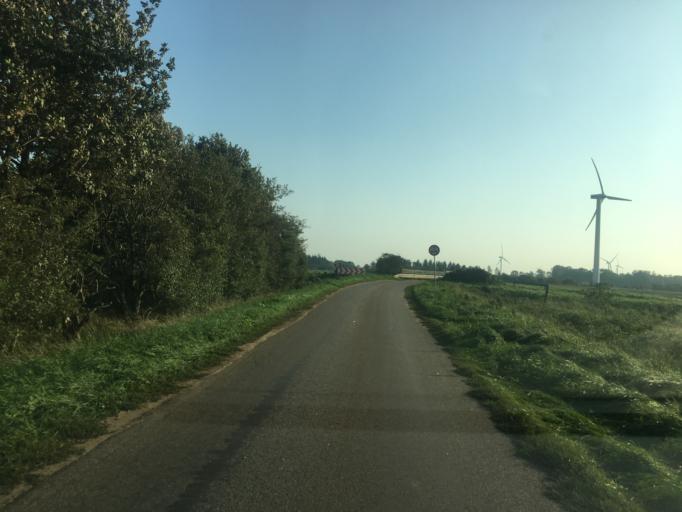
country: DE
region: Schleswig-Holstein
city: Ellhoft
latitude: 54.9247
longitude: 8.9679
